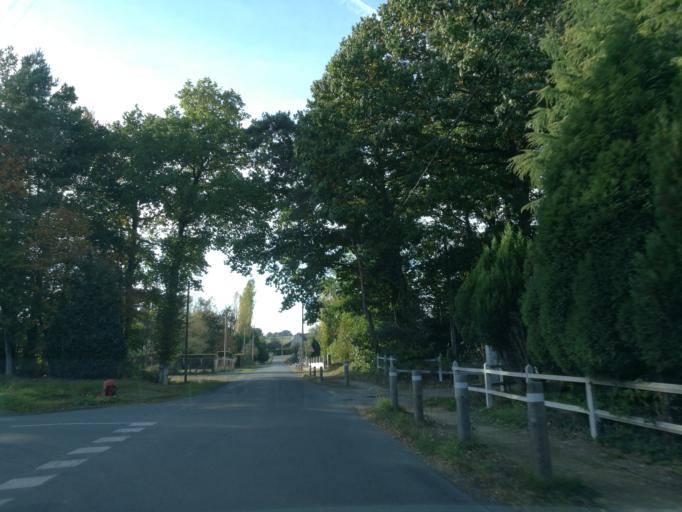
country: FR
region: Brittany
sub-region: Departement d'Ille-et-Vilaine
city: Bedee
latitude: 48.1882
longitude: -1.9449
